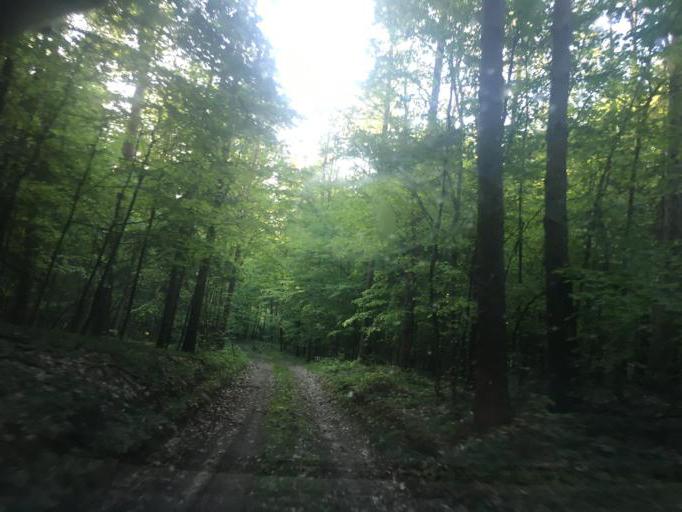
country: PL
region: Kujawsko-Pomorskie
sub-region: Powiat brodnicki
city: Gorzno
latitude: 53.2154
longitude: 19.7280
